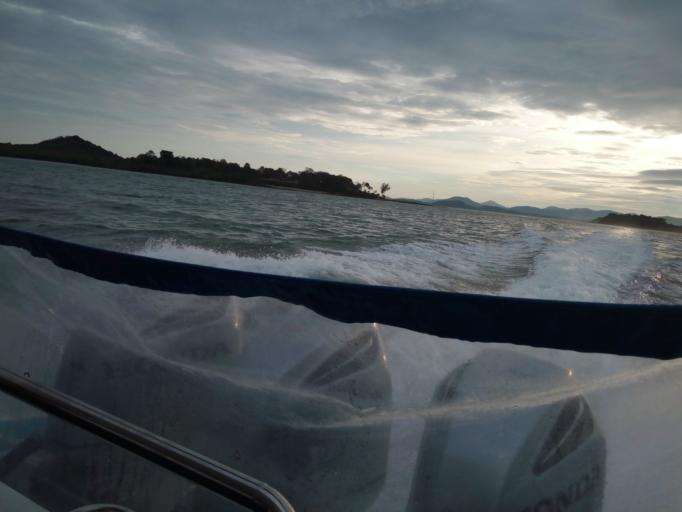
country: TH
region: Phuket
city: Thalang
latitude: 8.0658
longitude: 98.4598
